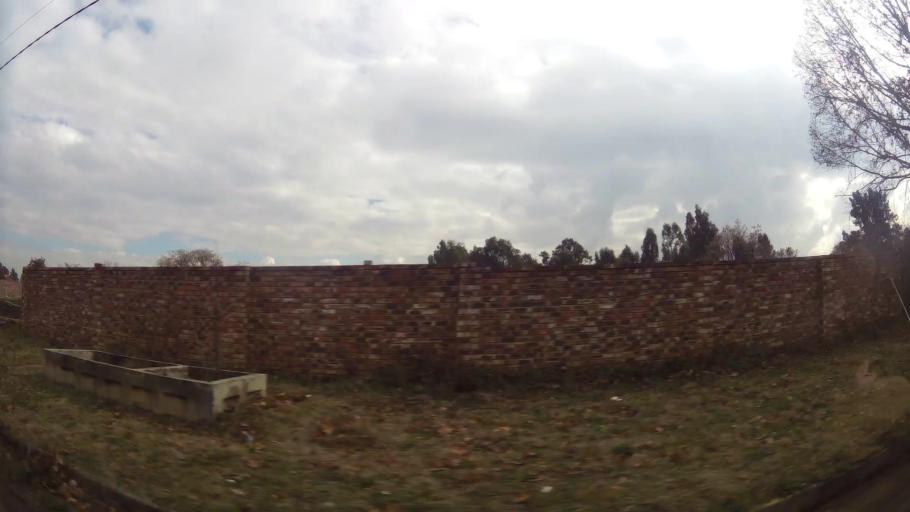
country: ZA
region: Gauteng
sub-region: Sedibeng District Municipality
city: Meyerton
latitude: -26.6003
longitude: 27.9995
